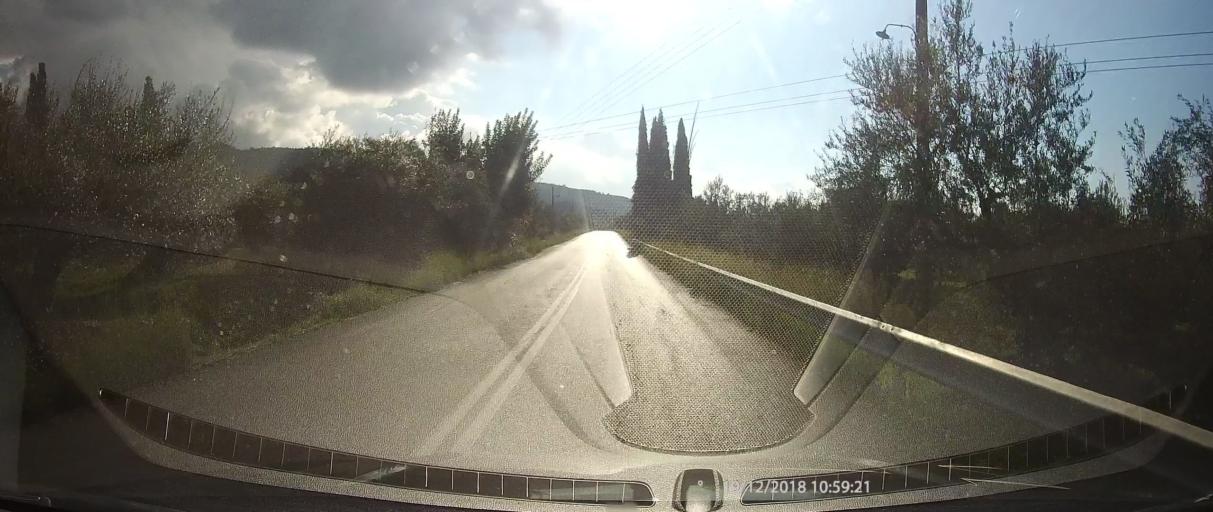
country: GR
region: Peloponnese
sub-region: Nomos Messinias
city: Kardamyli
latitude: 36.8969
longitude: 22.2284
